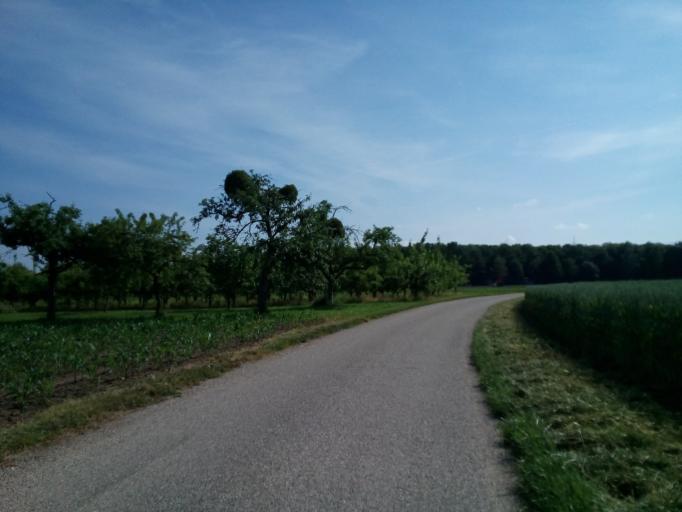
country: DE
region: Baden-Wuerttemberg
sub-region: Freiburg Region
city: Rheinau
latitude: 48.6451
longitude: 7.9343
